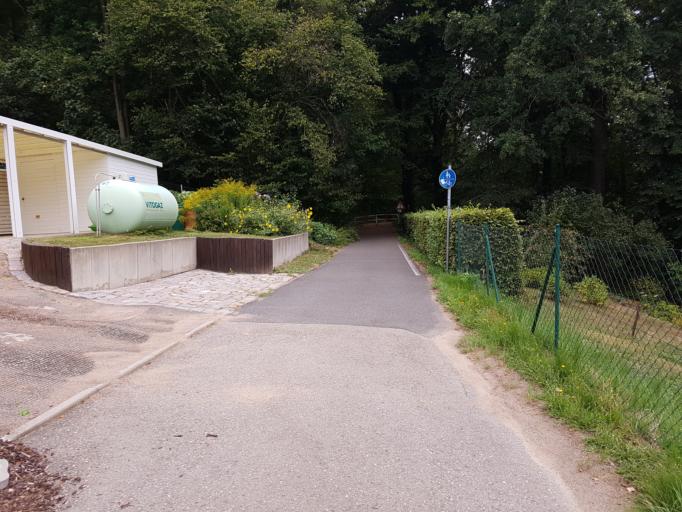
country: DE
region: Saxony
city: Kriebstein
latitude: 51.0579
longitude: 13.0198
